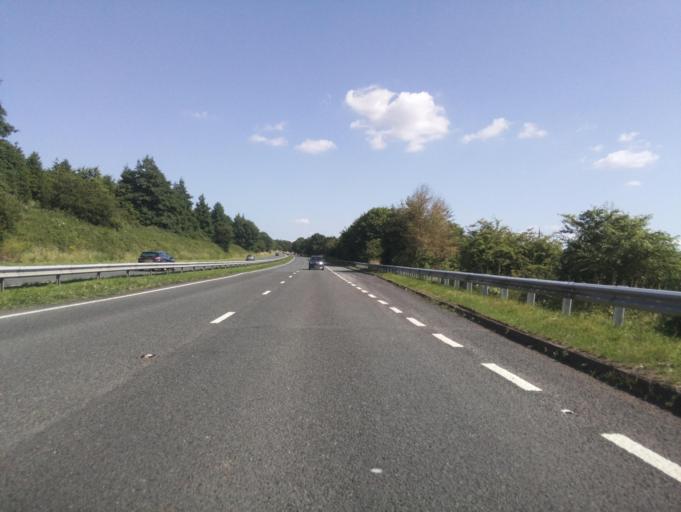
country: GB
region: England
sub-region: Worcestershire
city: Barnt Green
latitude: 52.3264
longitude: -2.0132
